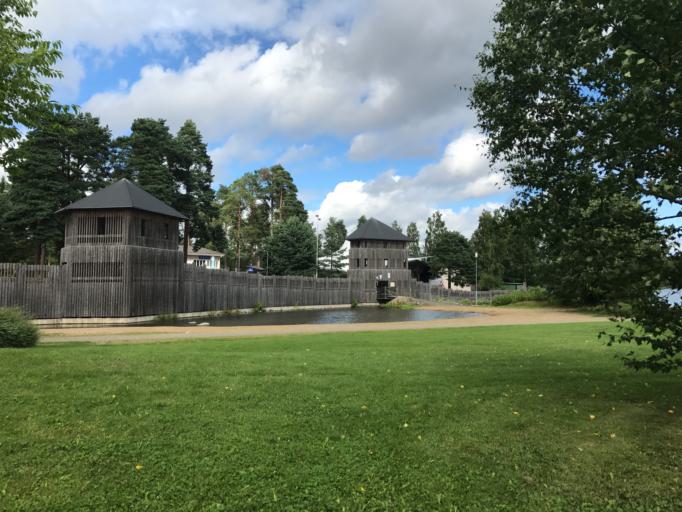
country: FI
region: Pirkanmaa
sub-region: Etelae-Pirkanmaa
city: Valkeakoski
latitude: 61.2673
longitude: 24.0410
